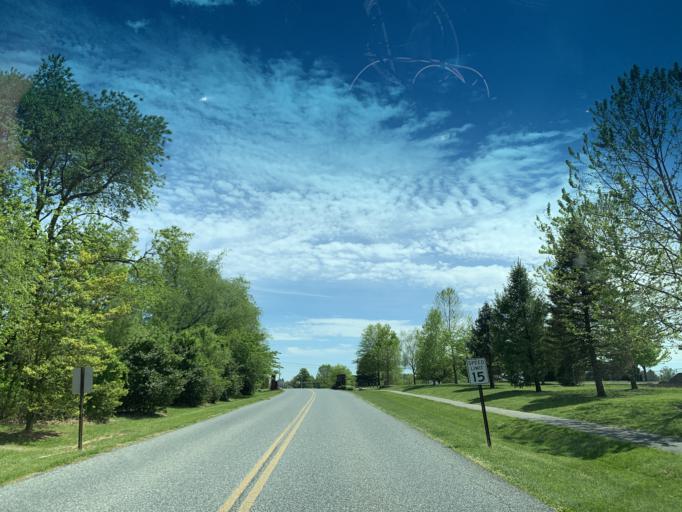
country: US
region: Maryland
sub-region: Harford County
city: South Bel Air
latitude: 39.5575
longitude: -76.2791
